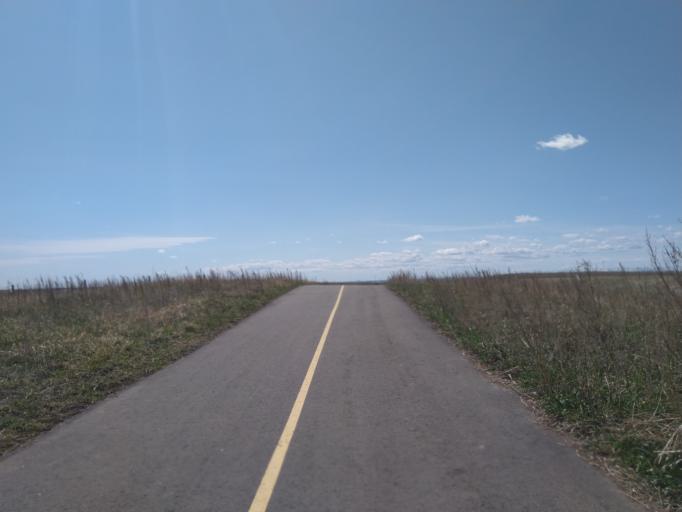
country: CA
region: Alberta
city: Chestermere
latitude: 51.0270
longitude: -113.9234
